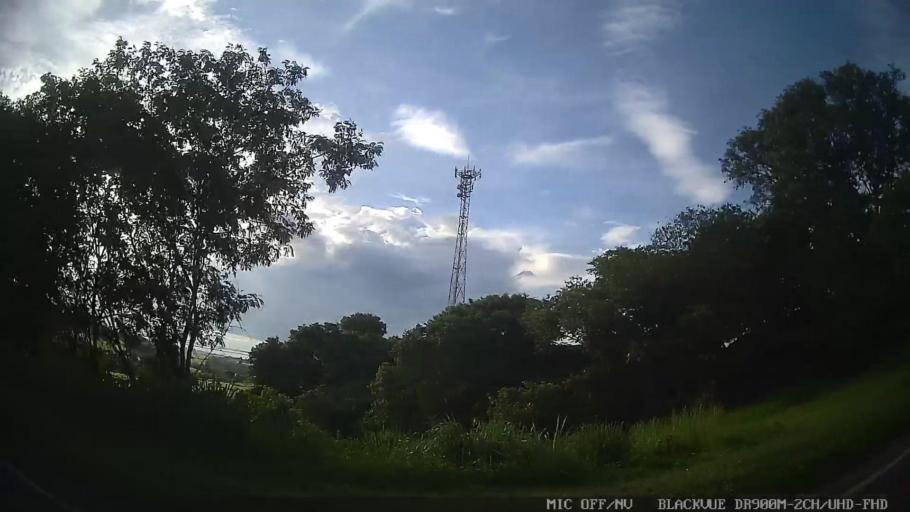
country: BR
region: Sao Paulo
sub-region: Tiete
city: Tiete
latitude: -23.0874
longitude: -47.7193
